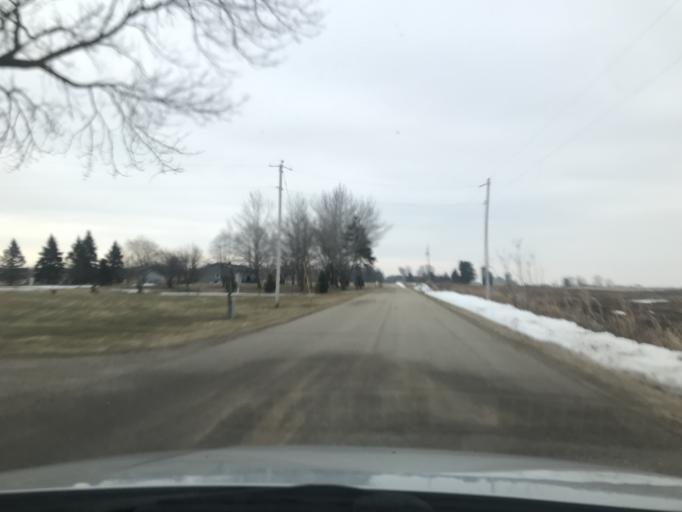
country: US
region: Wisconsin
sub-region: Marinette County
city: Peshtigo
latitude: 45.1252
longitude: -88.0078
